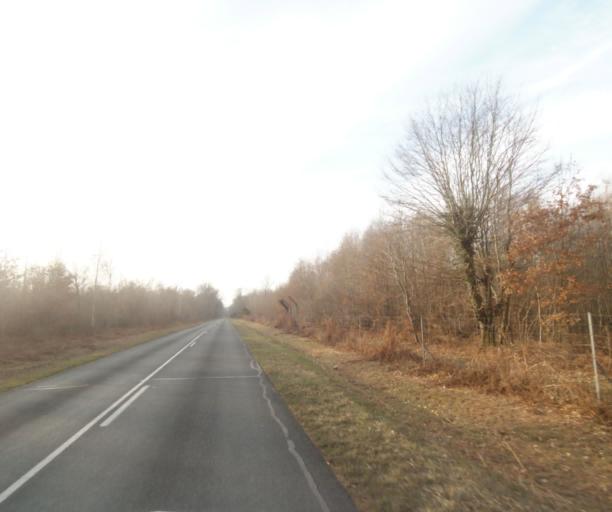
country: FR
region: Champagne-Ardenne
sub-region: Departement de la Haute-Marne
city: Bettancourt-la-Ferree
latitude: 48.6863
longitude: 4.9436
